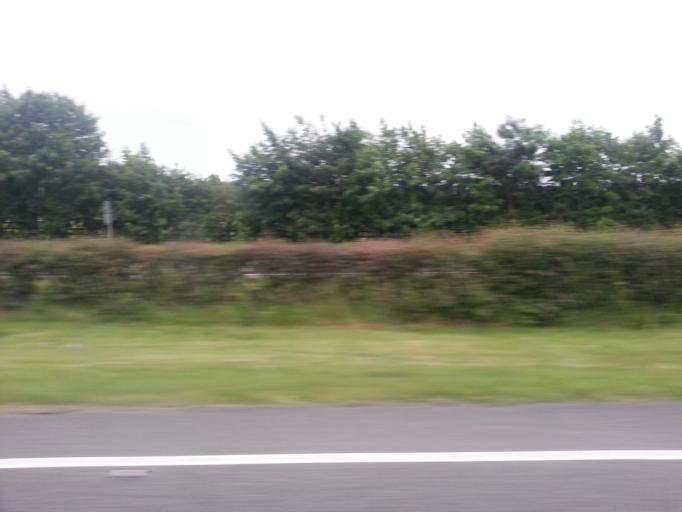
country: IE
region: Leinster
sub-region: Kildare
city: Naas
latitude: 53.2179
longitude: -6.7020
